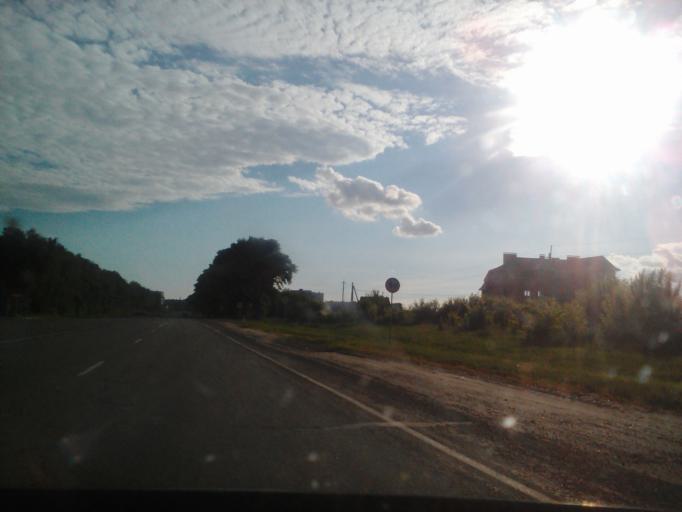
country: RU
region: Kursk
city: Kurchatov
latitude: 51.6589
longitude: 35.7117
